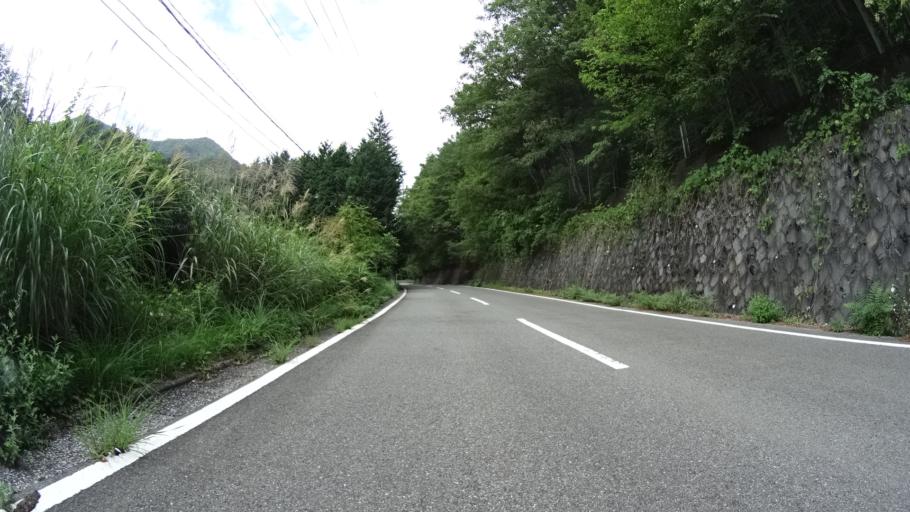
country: JP
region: Yamanashi
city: Kofu-shi
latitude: 35.7669
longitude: 138.5498
